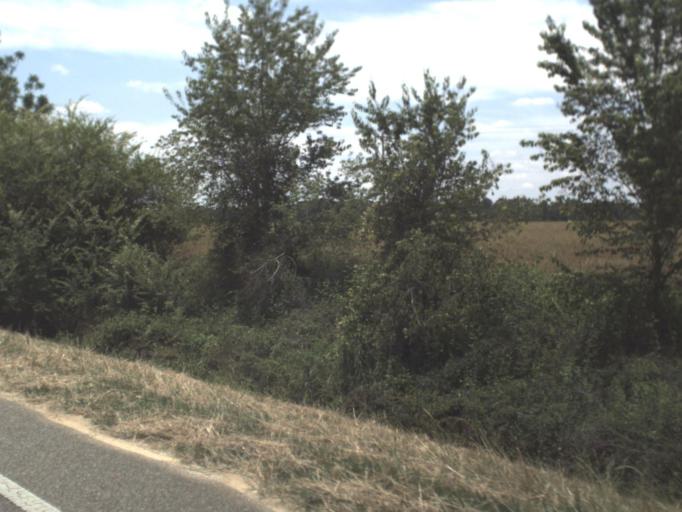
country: US
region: Florida
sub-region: Calhoun County
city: Blountstown
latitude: 30.5397
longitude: -85.1312
